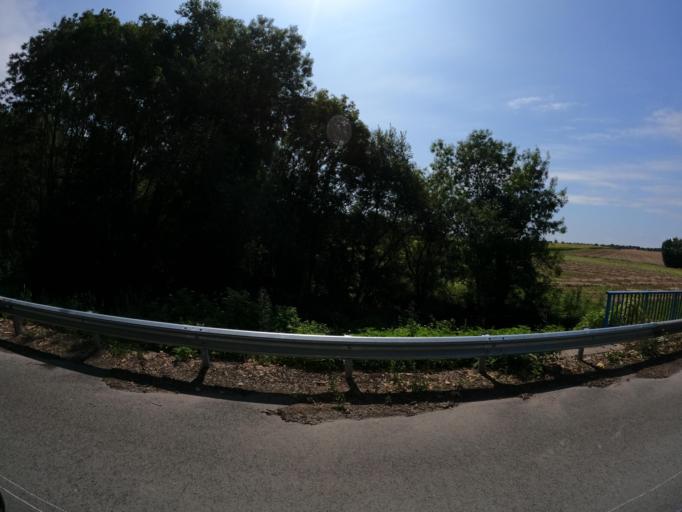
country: FR
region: Poitou-Charentes
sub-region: Departement des Deux-Sevres
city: Mauze-sur-le-Mignon
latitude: 46.2067
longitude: -0.6398
